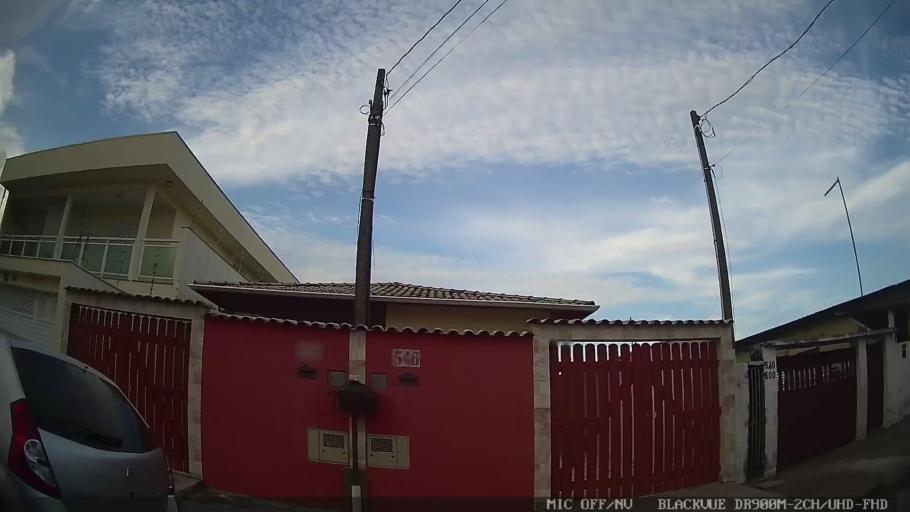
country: BR
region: Sao Paulo
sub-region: Itanhaem
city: Itanhaem
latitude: -24.1682
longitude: -46.7766
